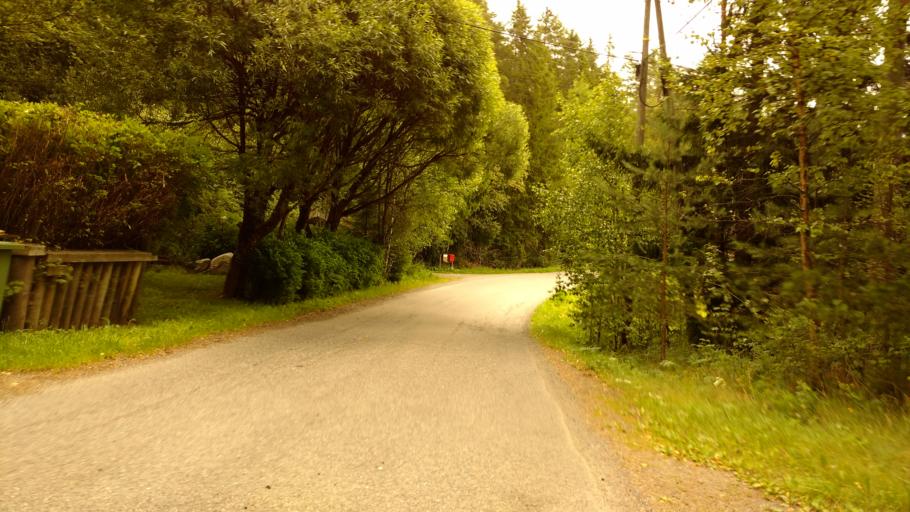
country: FI
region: Varsinais-Suomi
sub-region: Turku
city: Lieto
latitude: 60.4408
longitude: 22.4367
